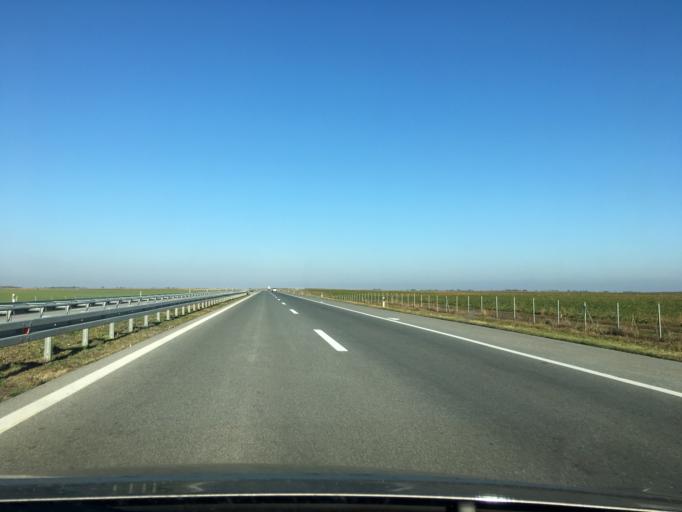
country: RS
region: Autonomna Pokrajina Vojvodina
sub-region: Severnobacki Okrug
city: Mali Igos
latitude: 45.7138
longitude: 19.7133
